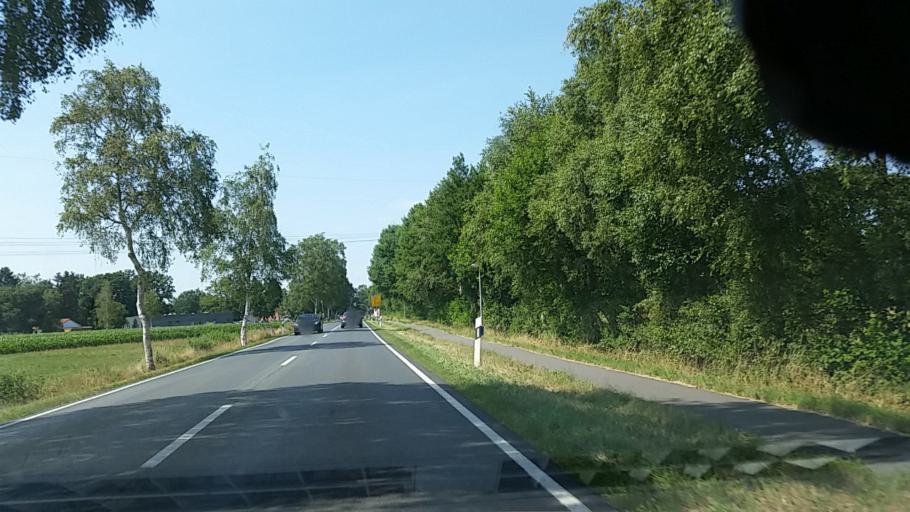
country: DE
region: Lower Saxony
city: Ottersberg
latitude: 53.0686
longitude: 9.1690
